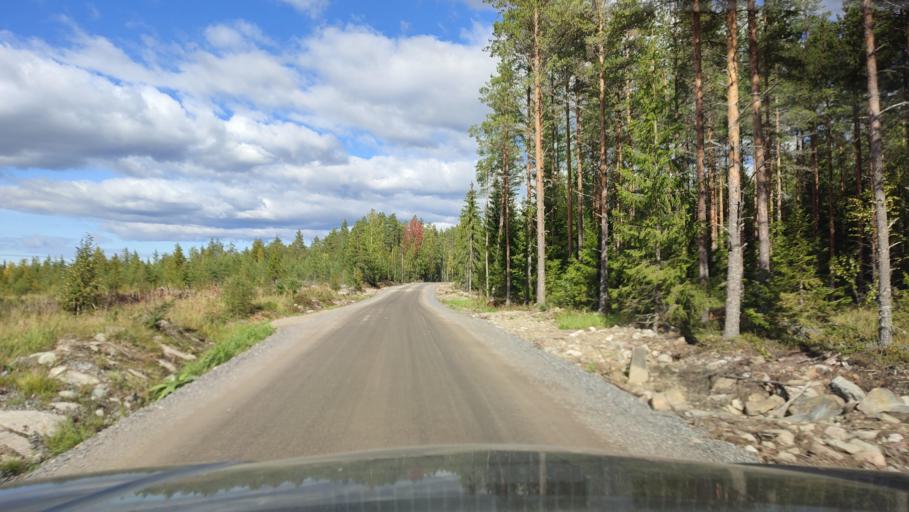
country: FI
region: Southern Ostrobothnia
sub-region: Suupohja
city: Karijoki
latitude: 62.1906
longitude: 21.5889
